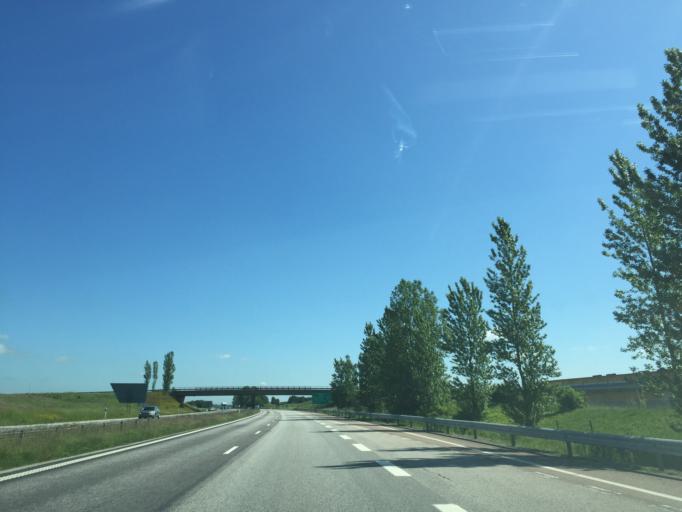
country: SE
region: Skane
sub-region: Helsingborg
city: Hyllinge
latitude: 56.1017
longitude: 12.8514
